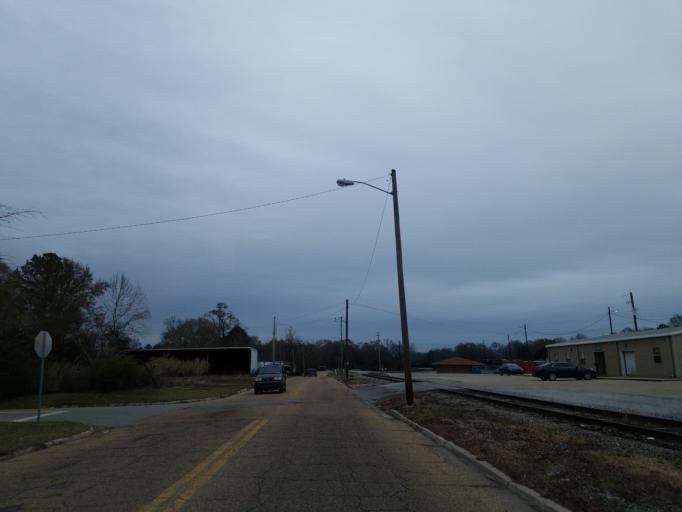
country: US
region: Mississippi
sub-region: Forrest County
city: Hattiesburg
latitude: 31.3298
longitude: -89.2858
